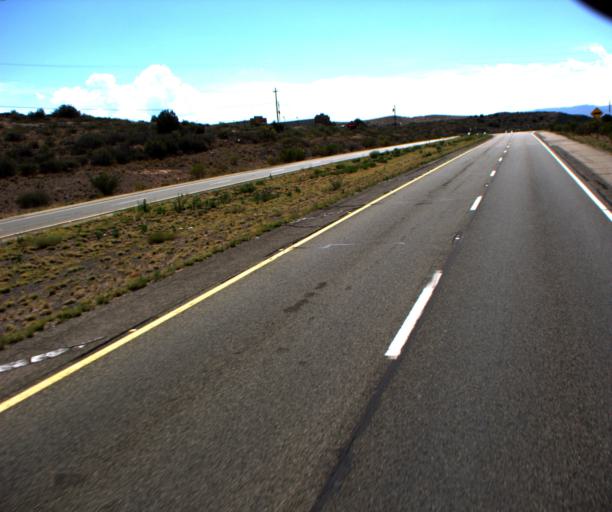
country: US
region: Arizona
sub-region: Yavapai County
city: Spring Valley
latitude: 34.3717
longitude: -112.1853
